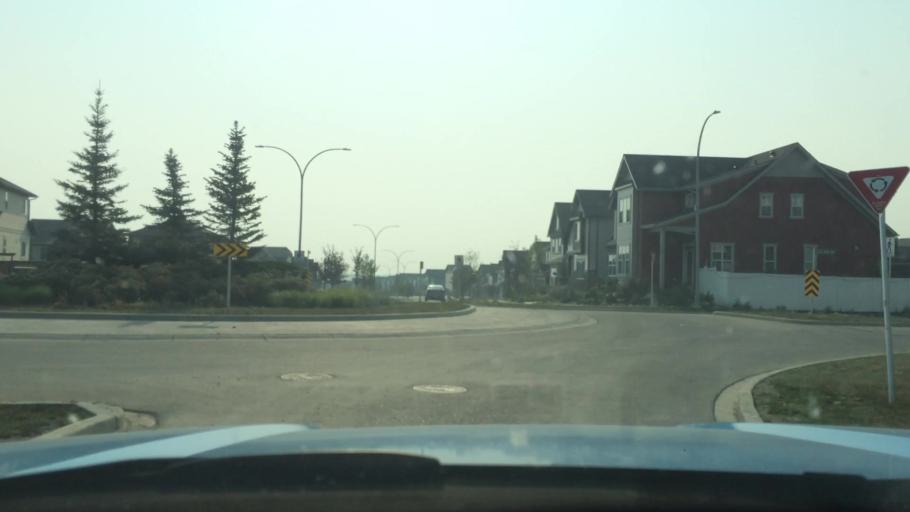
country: CA
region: Alberta
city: Calgary
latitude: 51.1802
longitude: -114.1574
